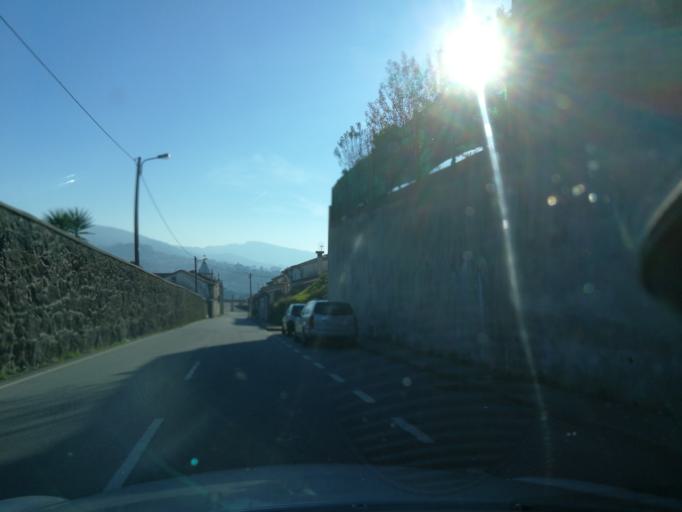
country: PT
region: Braga
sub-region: Braga
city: Adaufe
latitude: 41.5702
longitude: -8.3891
